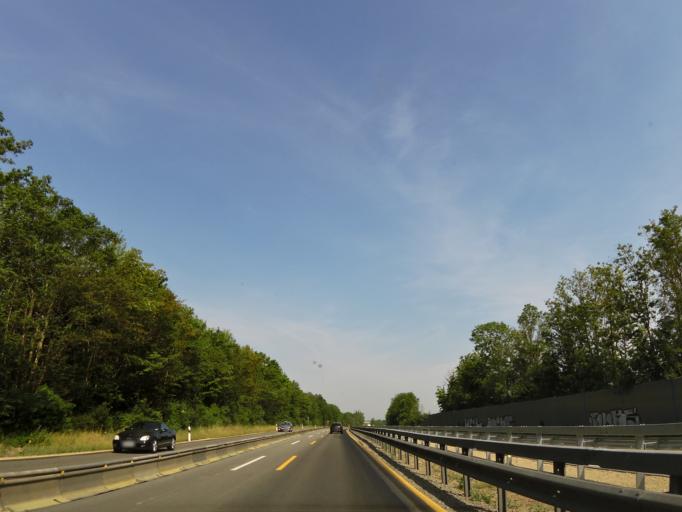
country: DE
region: Rheinland-Pfalz
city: Dintesheim
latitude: 49.7123
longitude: 8.1425
